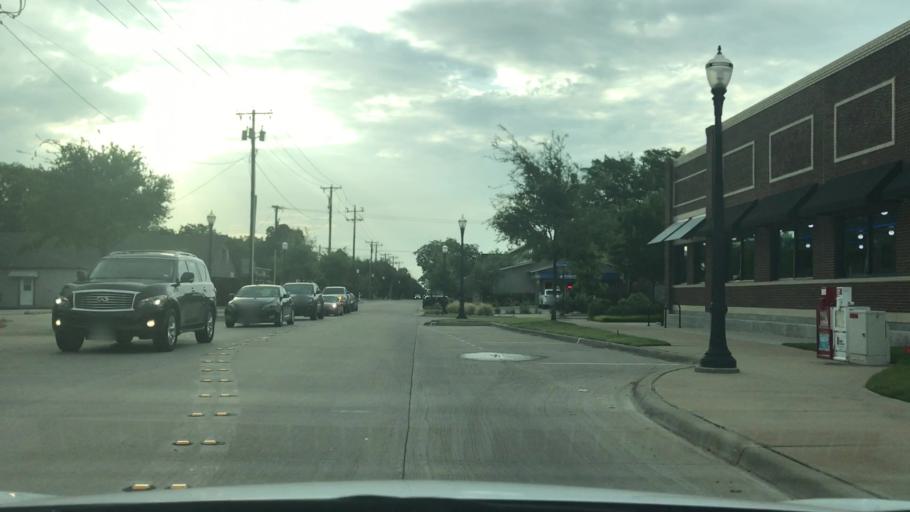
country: US
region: Texas
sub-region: Dallas County
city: Coppell
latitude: 32.9547
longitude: -97.0065
